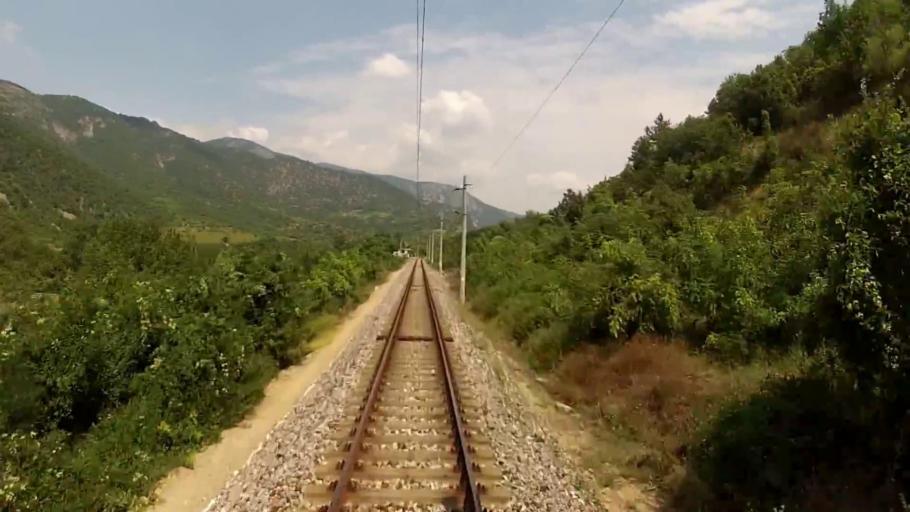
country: BG
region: Blagoevgrad
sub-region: Obshtina Kresna
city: Kresna
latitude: 41.7487
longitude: 23.1588
